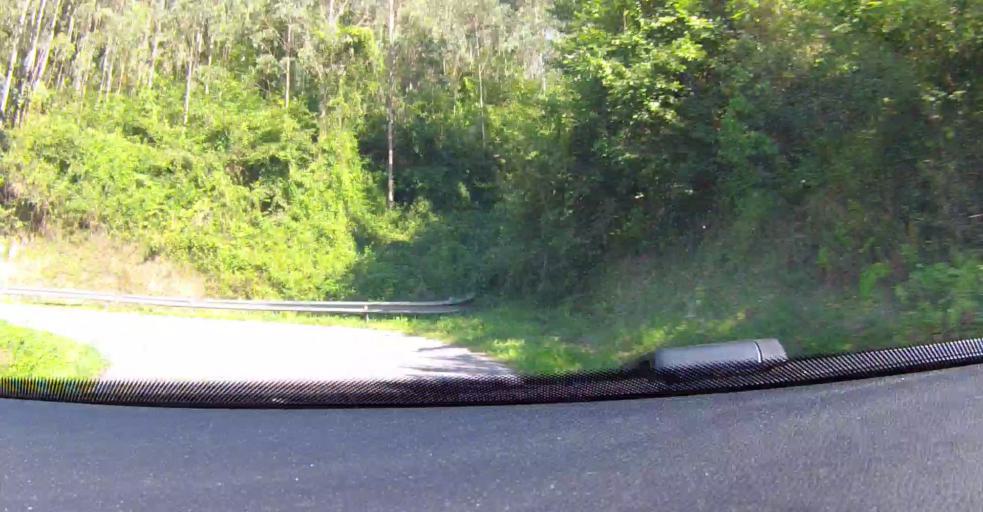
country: ES
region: Asturias
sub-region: Province of Asturias
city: Villaviciosa
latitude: 43.4840
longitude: -5.4216
